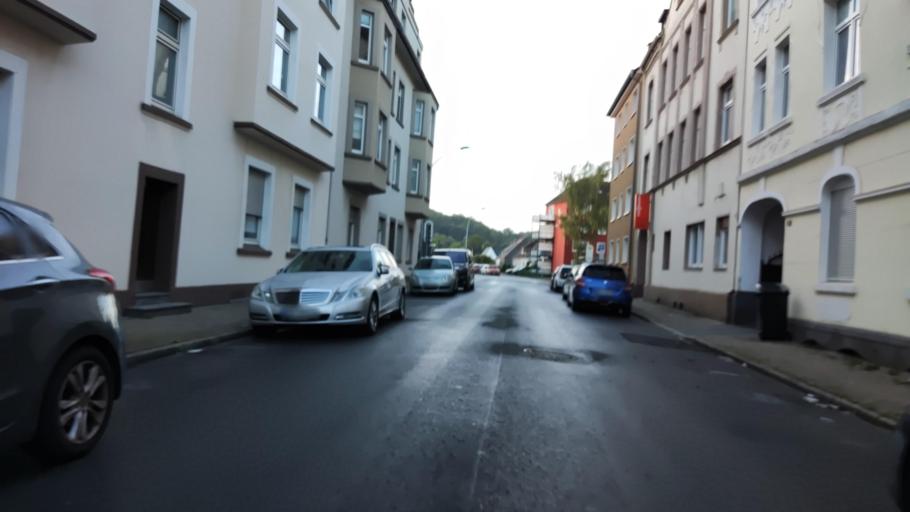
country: DE
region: North Rhine-Westphalia
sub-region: Regierungsbezirk Arnsberg
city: Herne
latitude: 51.5257
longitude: 7.2278
